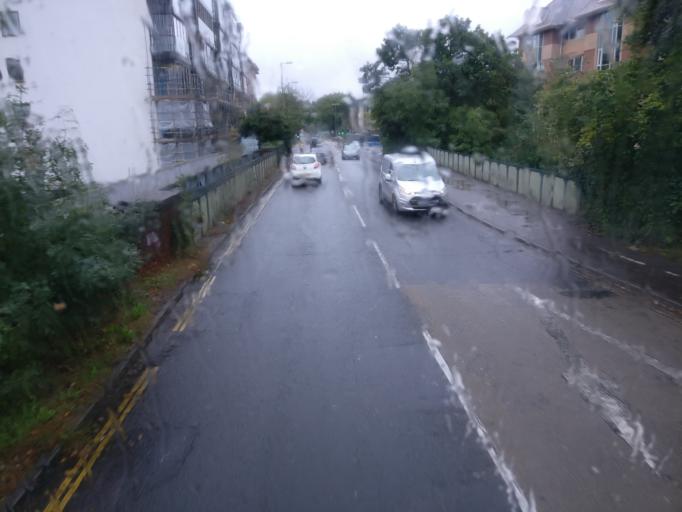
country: GB
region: England
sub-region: Hampshire
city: Farnborough
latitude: 51.2974
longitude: -0.7533
